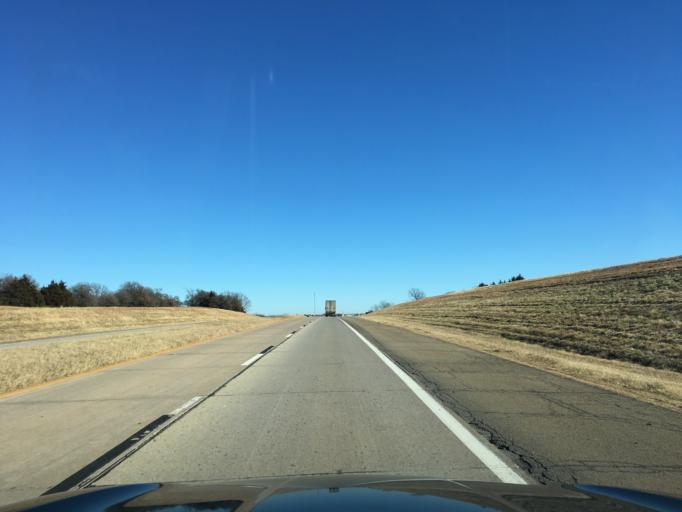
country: US
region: Oklahoma
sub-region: Pawnee County
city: Pawnee
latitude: 36.2248
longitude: -96.7739
